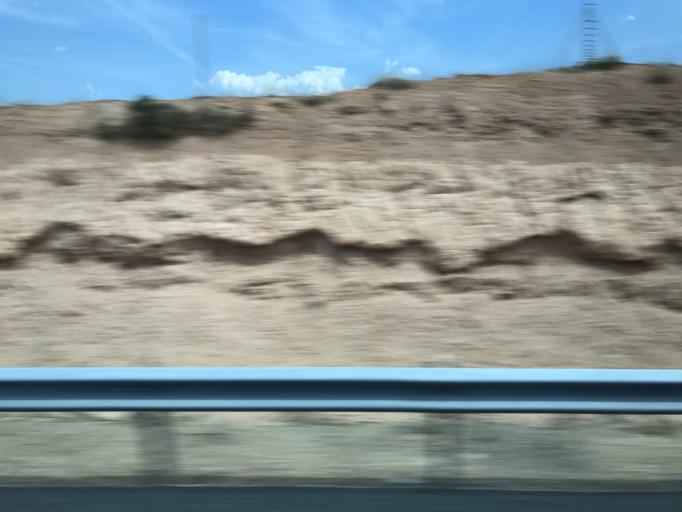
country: ES
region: Castille and Leon
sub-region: Provincia de Burgos
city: Lerma
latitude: 42.0149
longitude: -3.7543
